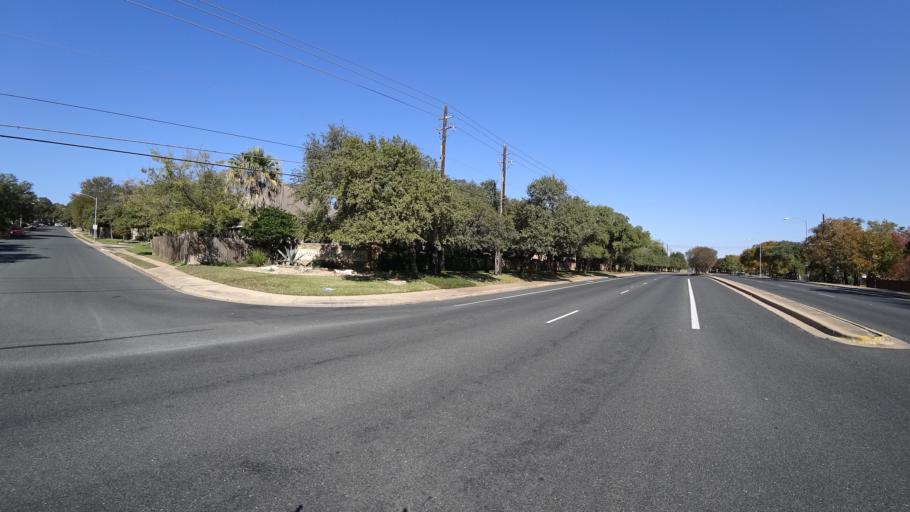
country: US
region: Texas
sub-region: Travis County
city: Barton Creek
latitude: 30.2274
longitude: -97.8677
